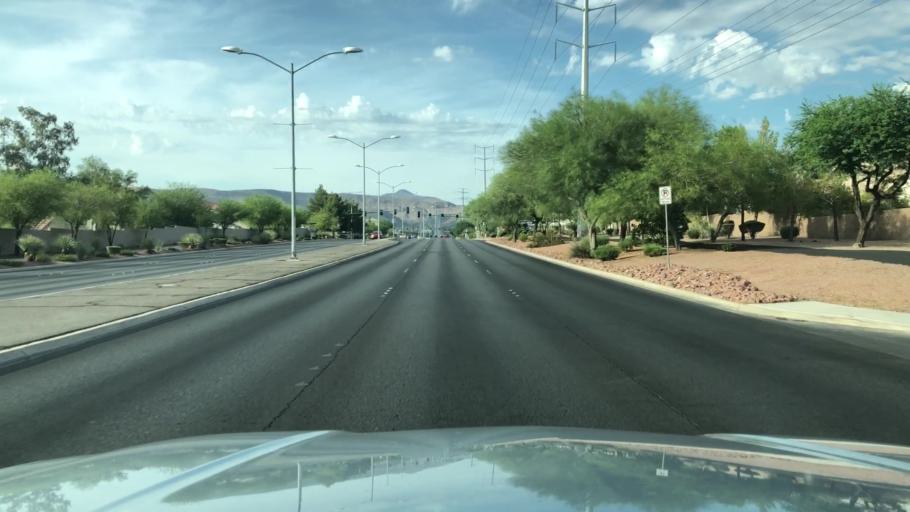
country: US
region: Nevada
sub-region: Clark County
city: Whitney
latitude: 36.0468
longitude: -115.0467
